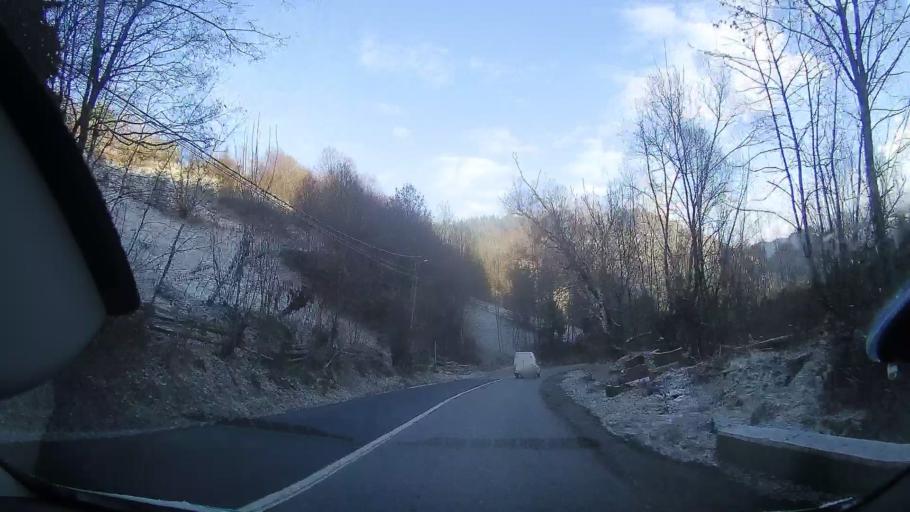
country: RO
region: Alba
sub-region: Comuna Scarisoara
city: Scarisoara
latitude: 46.4604
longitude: 22.8804
